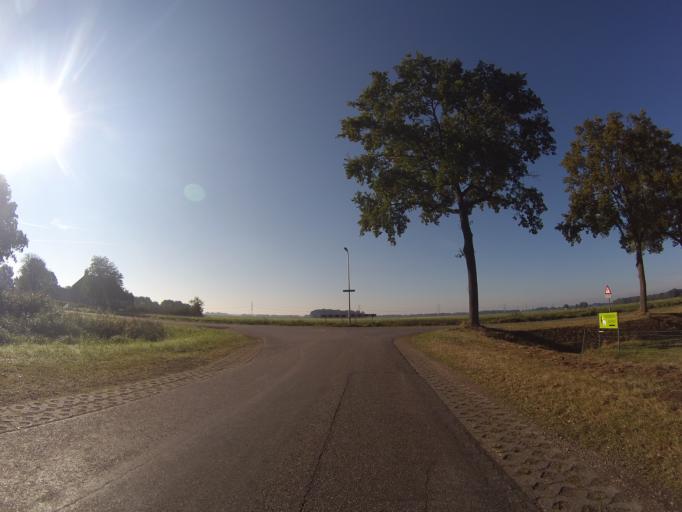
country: NL
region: Drenthe
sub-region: Gemeente Coevorden
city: Sleen
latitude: 52.7382
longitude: 6.7857
